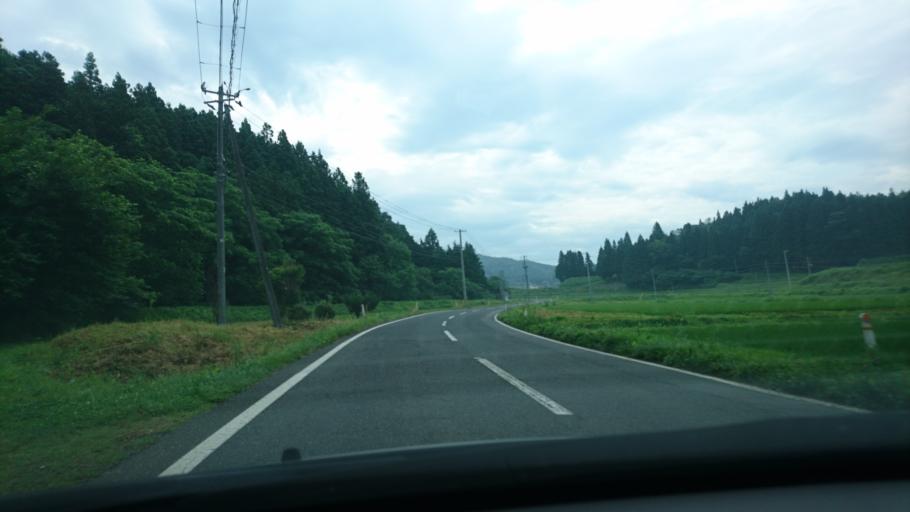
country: JP
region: Iwate
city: Ichinoseki
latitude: 38.9081
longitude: 141.4219
